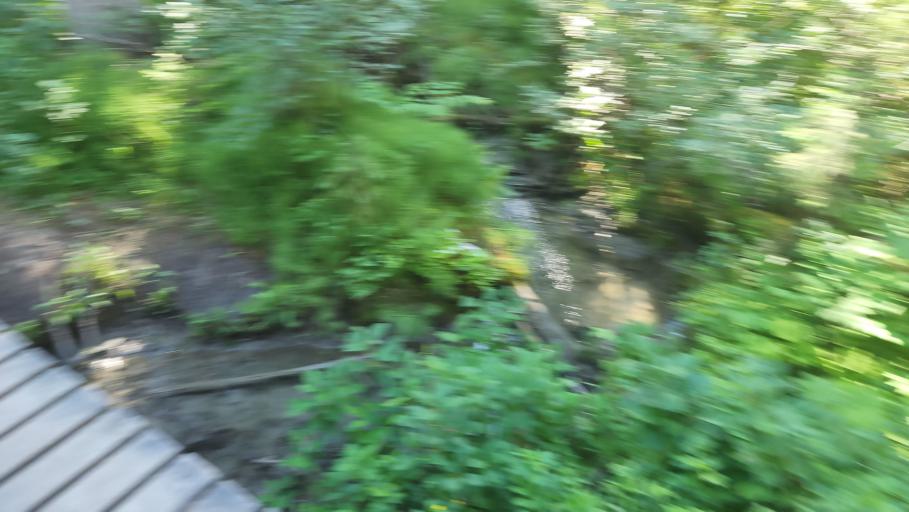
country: CA
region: Alberta
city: Lake Louise
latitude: 51.4367
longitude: -116.5307
